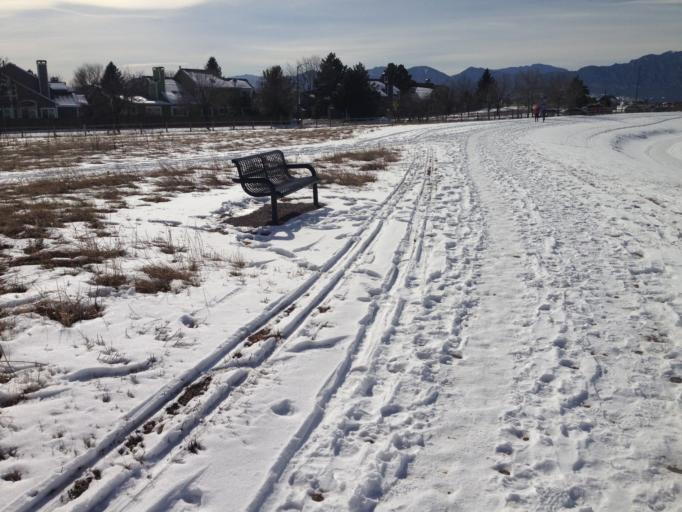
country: US
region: Colorado
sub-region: Boulder County
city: Superior
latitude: 39.9789
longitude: -105.1635
